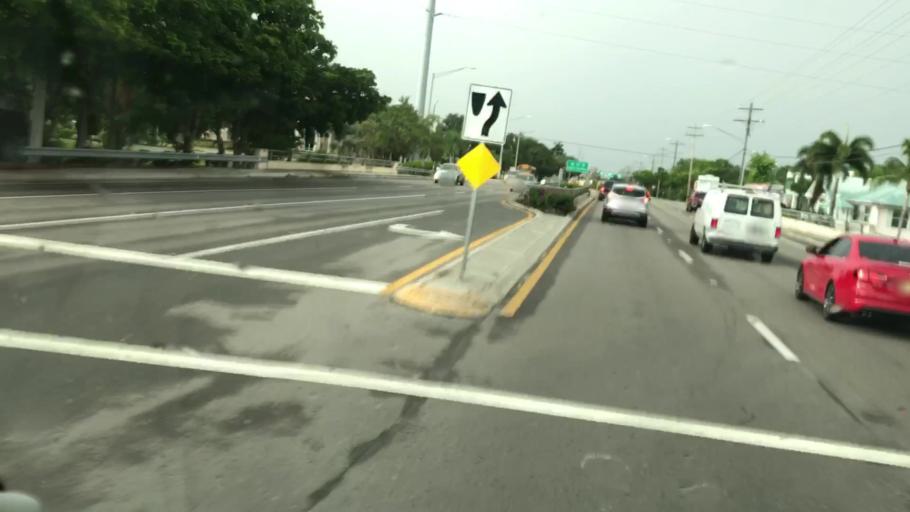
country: US
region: Florida
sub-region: Lee County
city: Cape Coral
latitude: 26.5995
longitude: -81.9415
